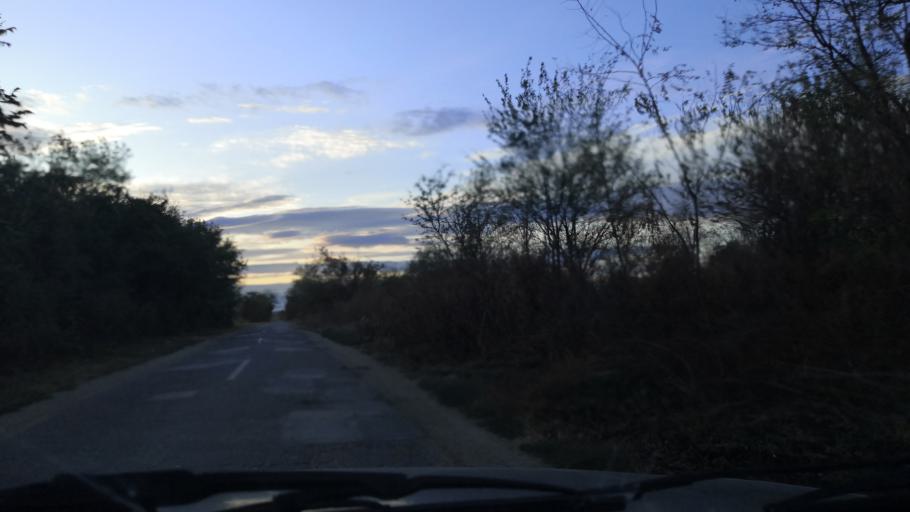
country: RO
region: Mehedinti
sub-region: Comuna Gruia
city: Izvoarele
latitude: 44.2752
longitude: 22.6609
